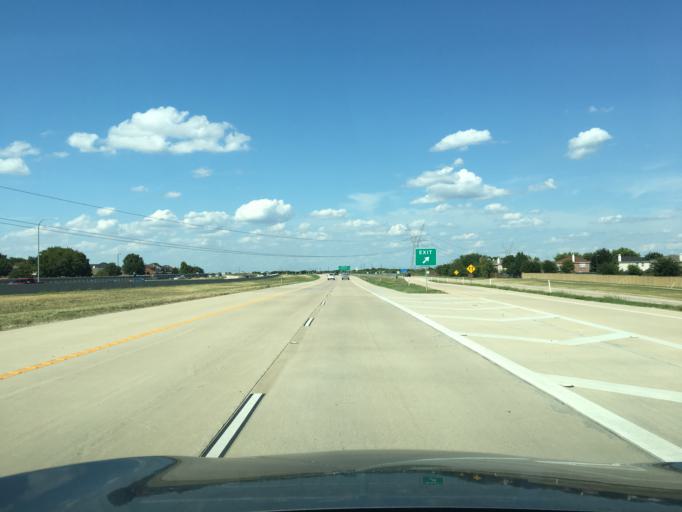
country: US
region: Texas
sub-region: Tarrant County
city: Mansfield
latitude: 32.6281
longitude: -97.0682
